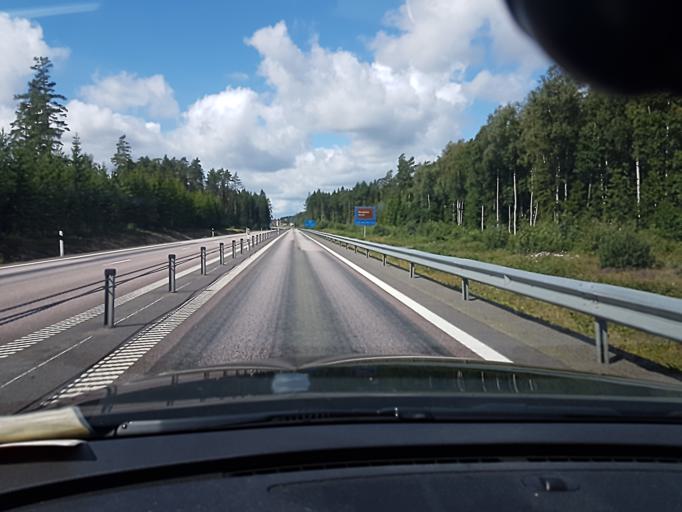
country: SE
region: Kalmar
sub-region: Emmaboda Kommun
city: Emmaboda
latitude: 56.7359
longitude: 15.4967
